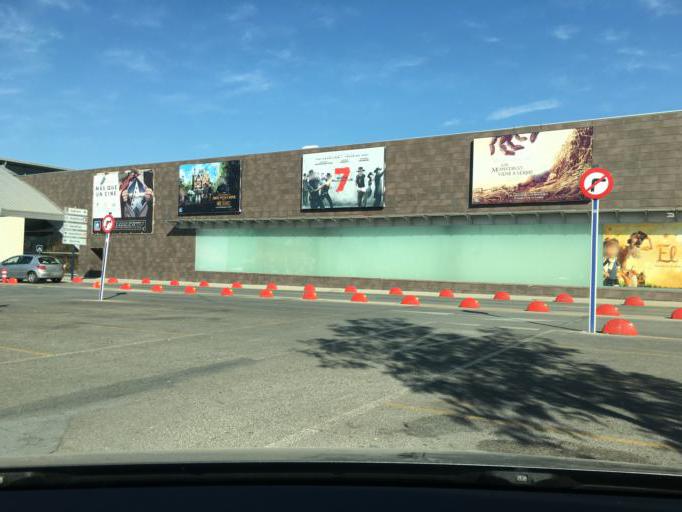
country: ES
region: Andalusia
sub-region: Provincia de Granada
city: Pulianas
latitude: 37.2141
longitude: -3.6158
